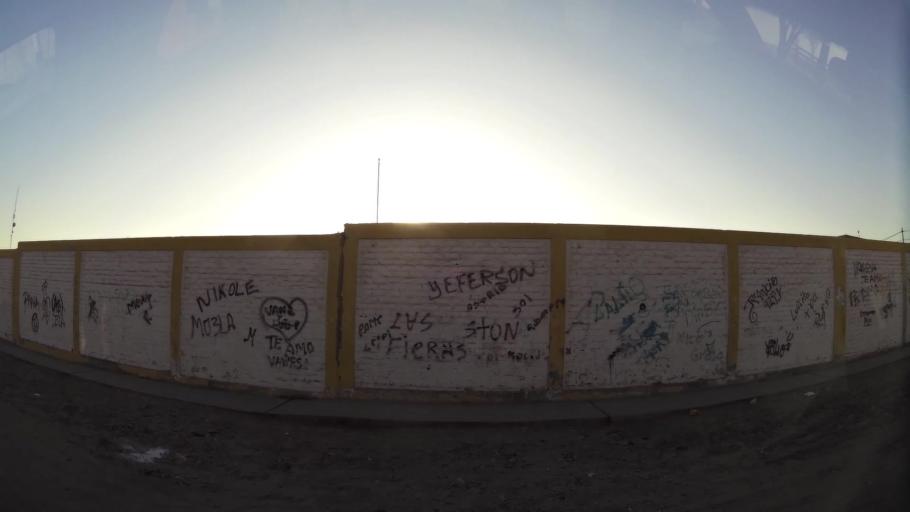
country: PE
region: Ica
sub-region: Provincia de Pisco
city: Villa Tupac Amaru
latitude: -13.7126
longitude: -76.1471
